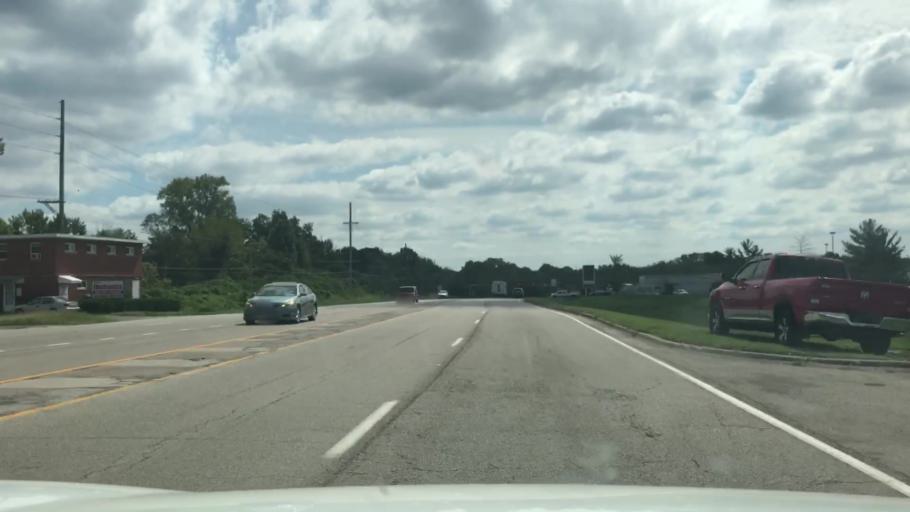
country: US
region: Illinois
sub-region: Saint Clair County
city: Swansea
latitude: 38.5464
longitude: -90.0537
